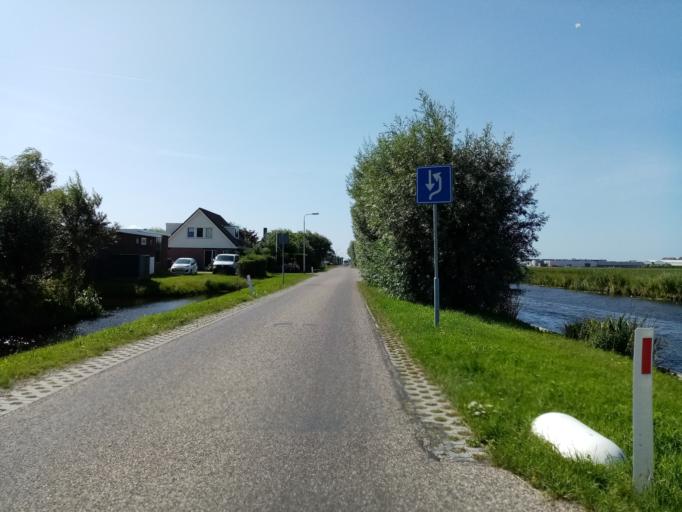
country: NL
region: South Holland
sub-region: Gemeente Hillegom
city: Hillegom
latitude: 52.3036
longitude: 4.5593
